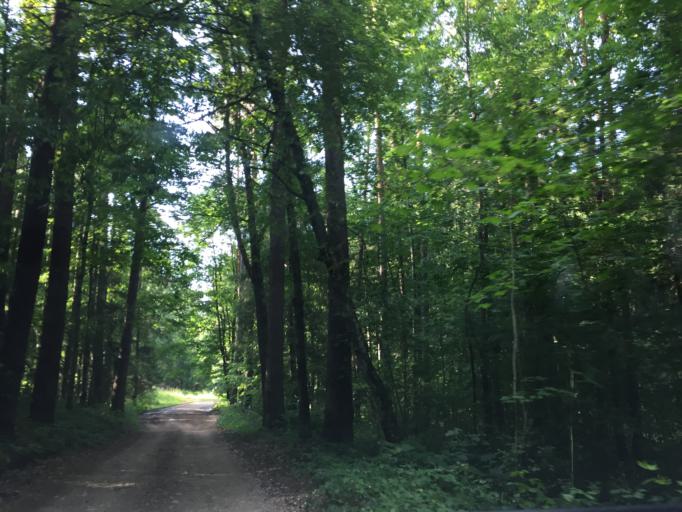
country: LV
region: Krimulda
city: Ragana
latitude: 57.1366
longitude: 24.7685
